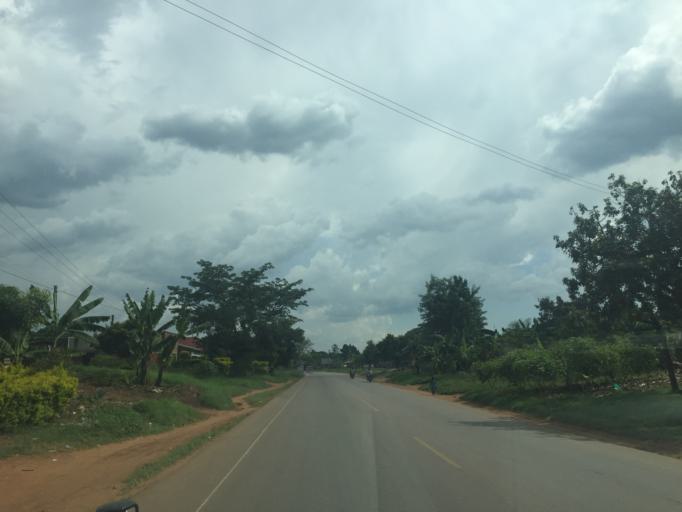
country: UG
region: Central Region
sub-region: Luwero District
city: Wobulenzi
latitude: 0.6873
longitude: 32.5229
